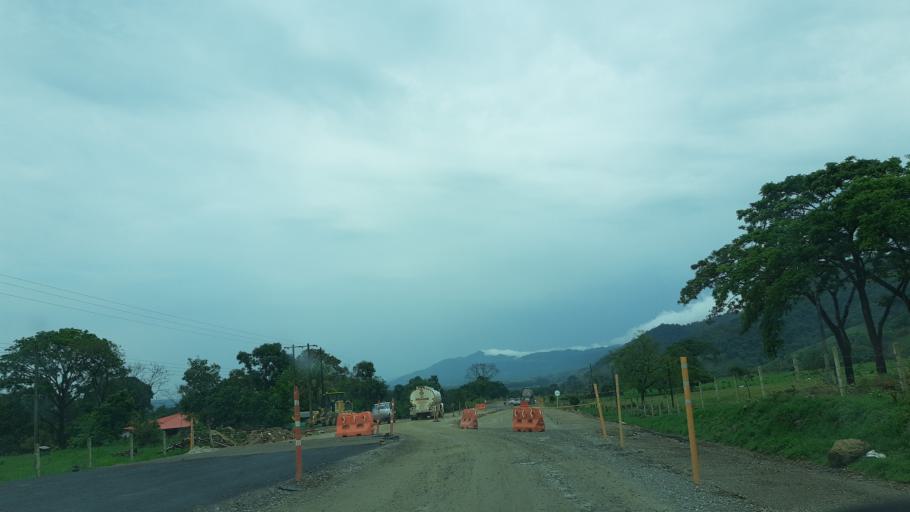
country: CO
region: Casanare
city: Monterrey
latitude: 4.8293
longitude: -72.9614
